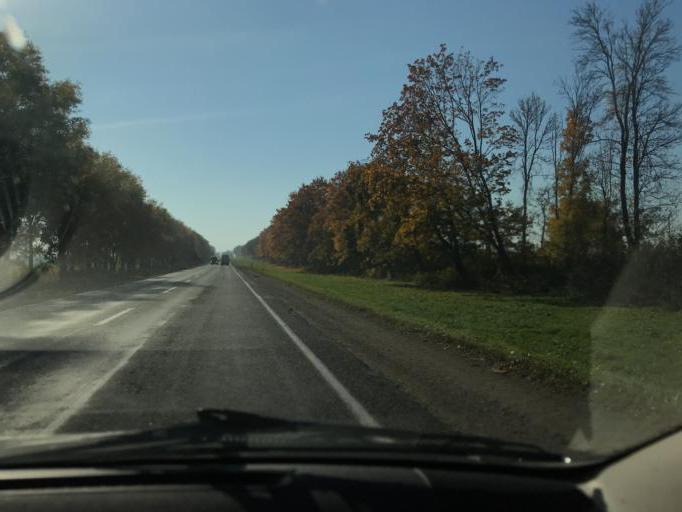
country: BY
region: Minsk
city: Salihorsk
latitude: 52.8869
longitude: 27.4707
